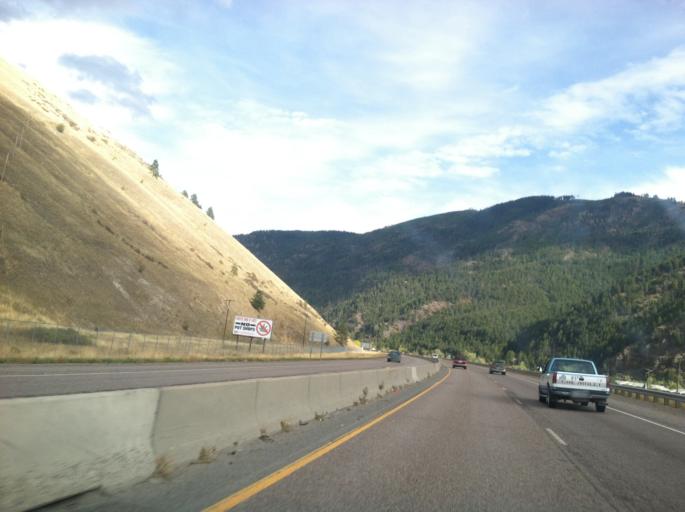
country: US
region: Montana
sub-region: Missoula County
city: Missoula
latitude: 46.8648
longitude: -113.9700
